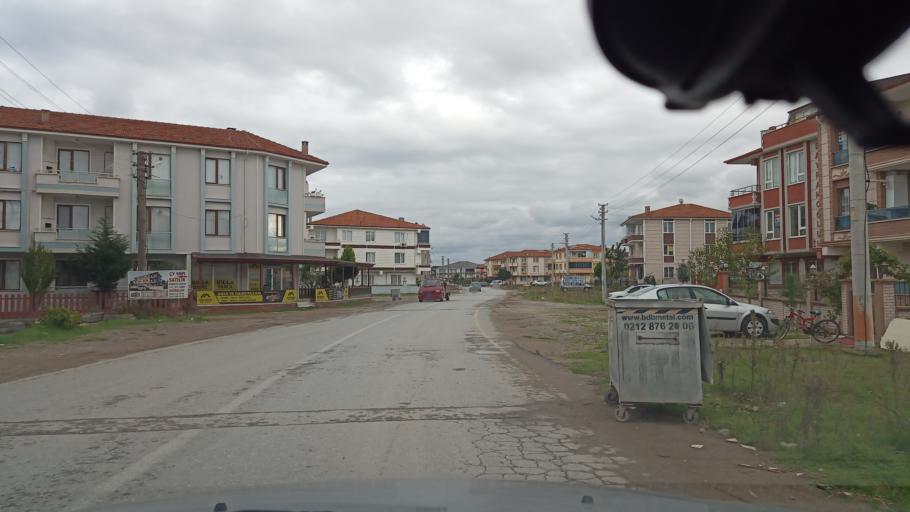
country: TR
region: Sakarya
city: Karasu
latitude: 41.1104
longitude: 30.6818
